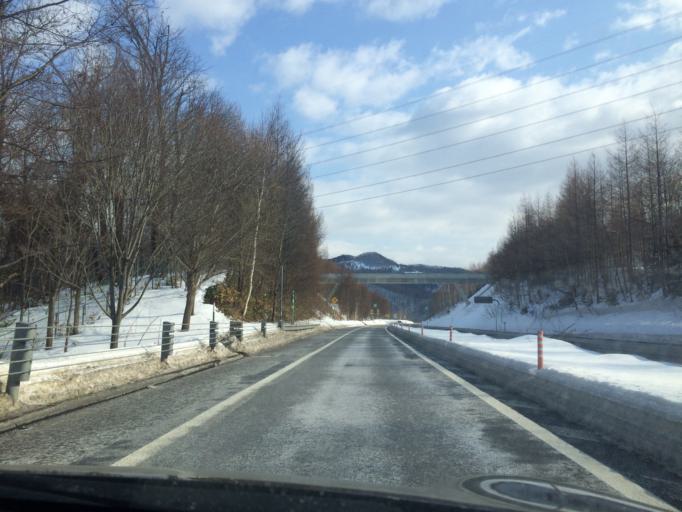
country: JP
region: Hokkaido
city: Chitose
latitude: 42.9114
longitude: 141.9078
